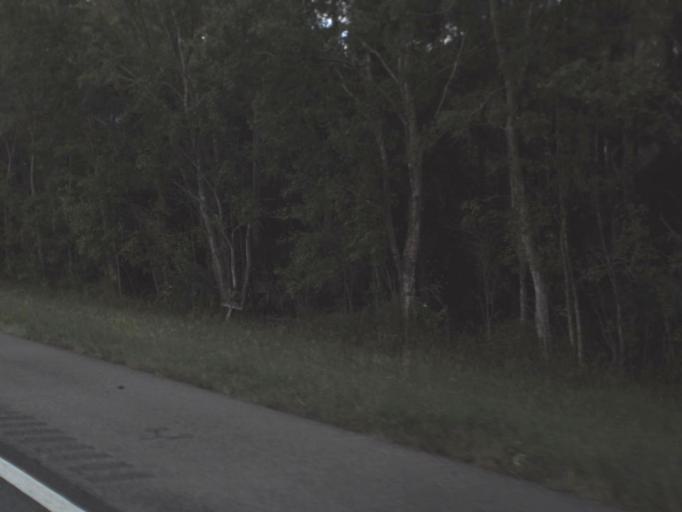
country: US
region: Florida
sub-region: Orange County
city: Christmas
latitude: 28.4526
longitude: -80.9395
